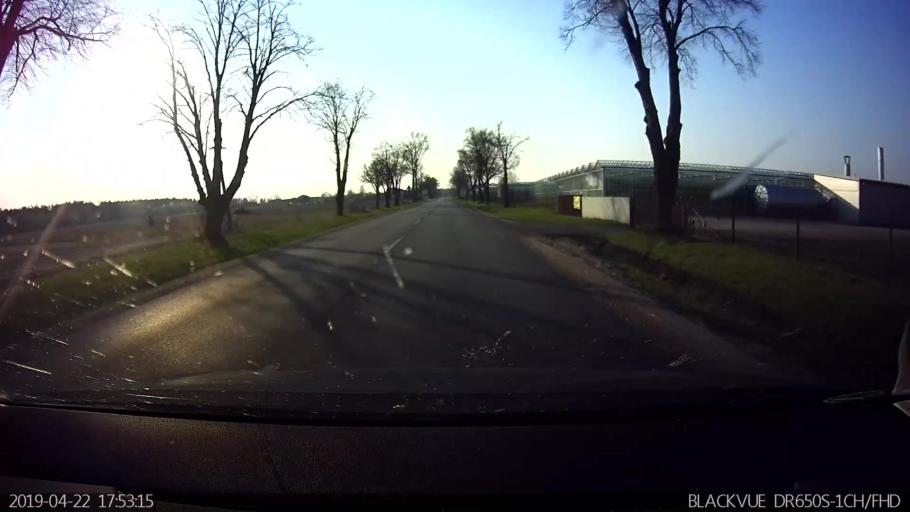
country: PL
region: Masovian Voivodeship
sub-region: Powiat wegrowski
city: Liw
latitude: 52.4513
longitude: 21.9581
